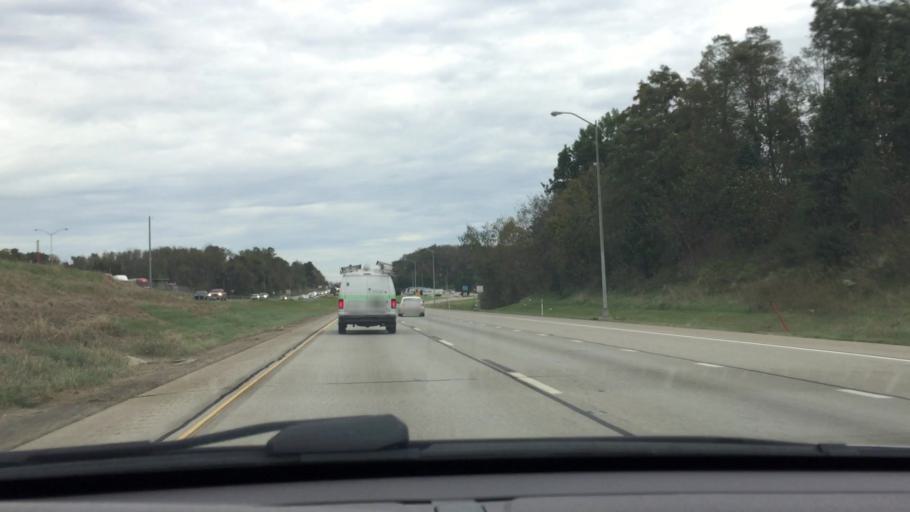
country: US
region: Pennsylvania
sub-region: Allegheny County
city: Bridgeville
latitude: 40.3273
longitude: -80.1412
